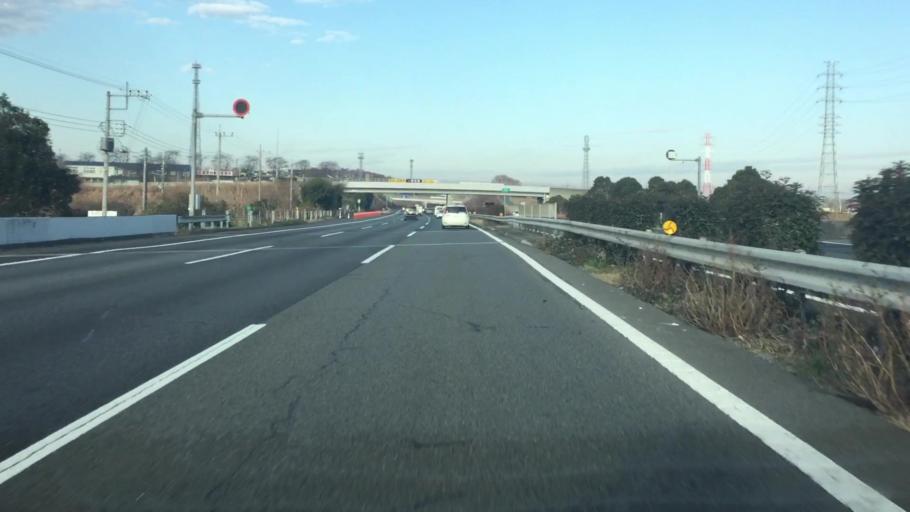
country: JP
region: Saitama
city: Yorii
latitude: 36.1621
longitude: 139.2075
